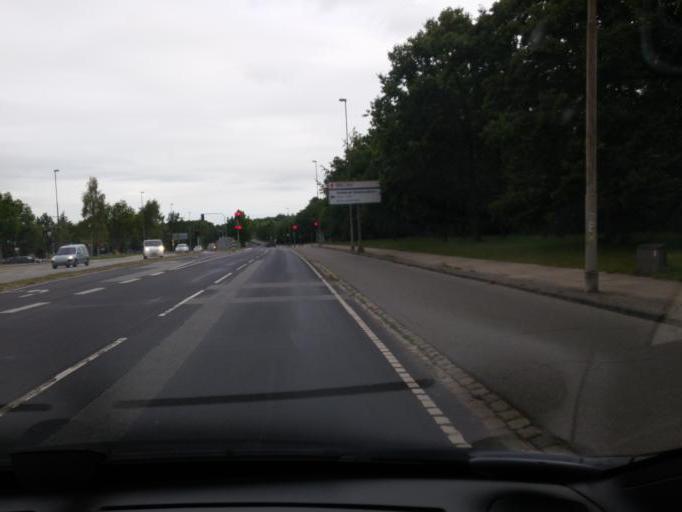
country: DK
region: South Denmark
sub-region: Odense Kommune
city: Seden
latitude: 55.4050
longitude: 10.4256
